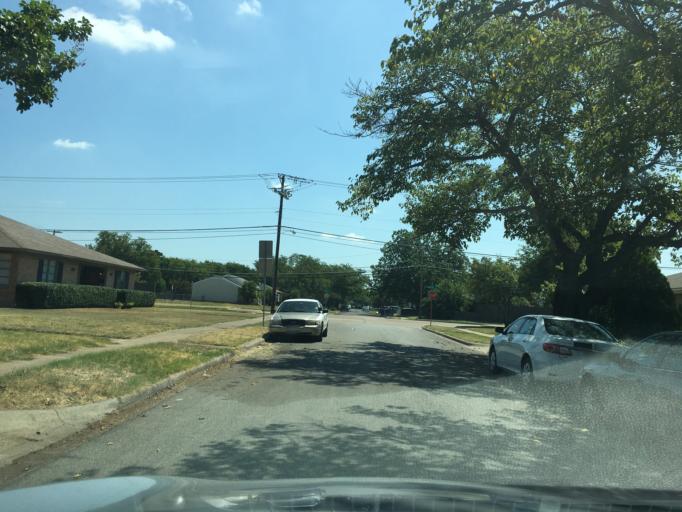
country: US
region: Texas
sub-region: Dallas County
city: Garland
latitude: 32.8524
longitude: -96.6838
